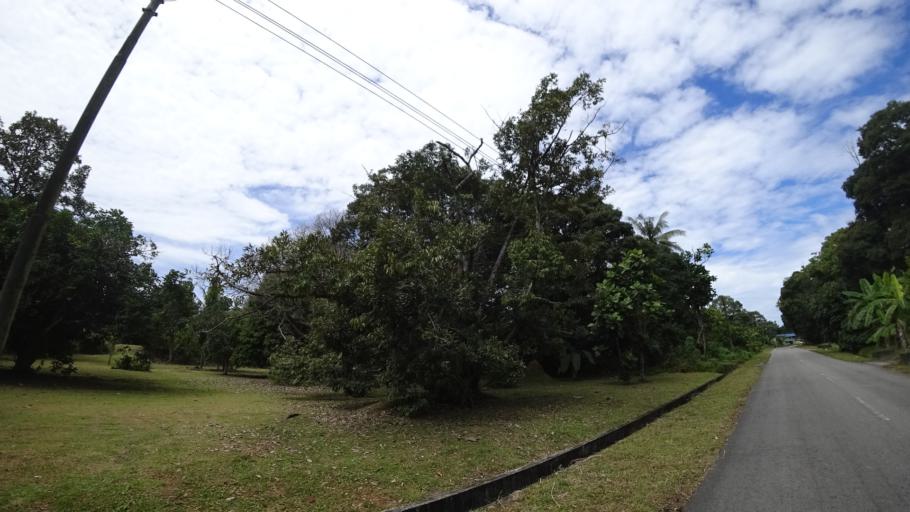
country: BN
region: Tutong
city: Tutong
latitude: 4.7692
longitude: 114.8215
